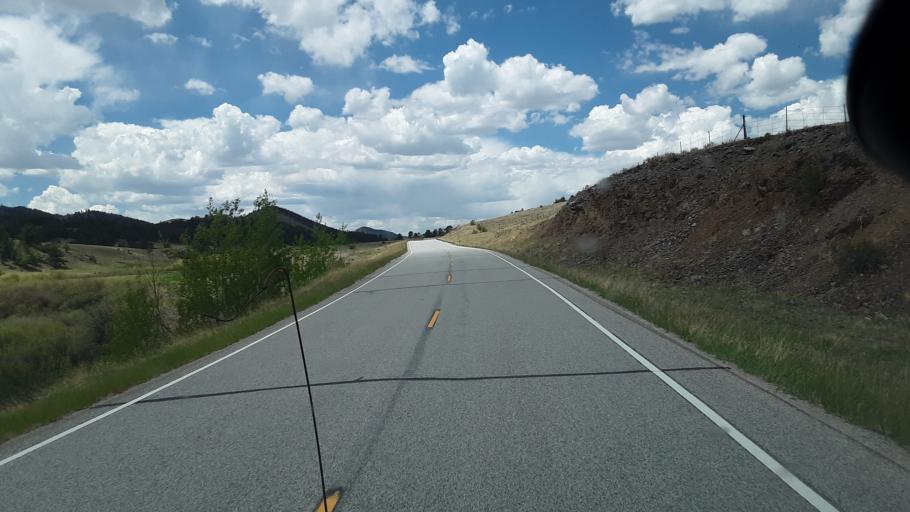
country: US
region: Colorado
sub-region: Teller County
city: Cripple Creek
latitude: 38.7886
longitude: -105.5859
